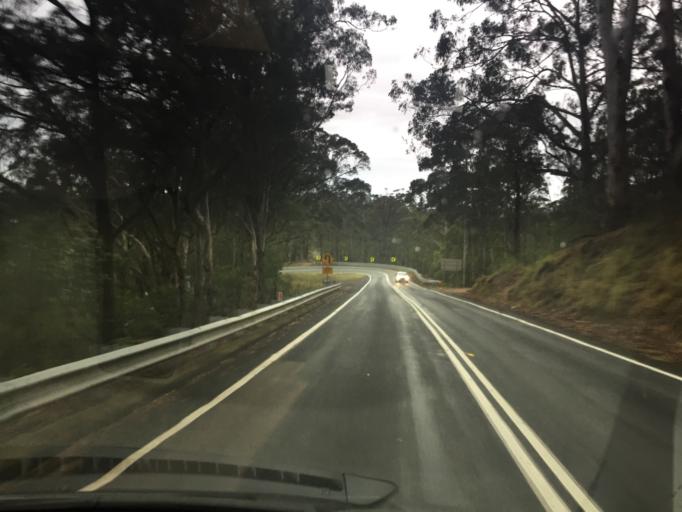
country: AU
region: New South Wales
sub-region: Bega Valley
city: Bega
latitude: -36.6116
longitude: 149.4765
